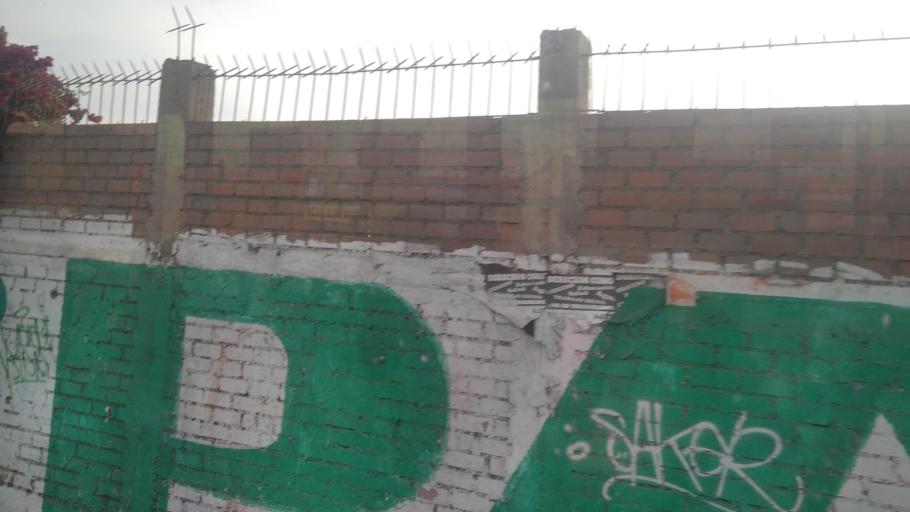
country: PE
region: Lima
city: Lima
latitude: -12.0186
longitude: -77.0019
